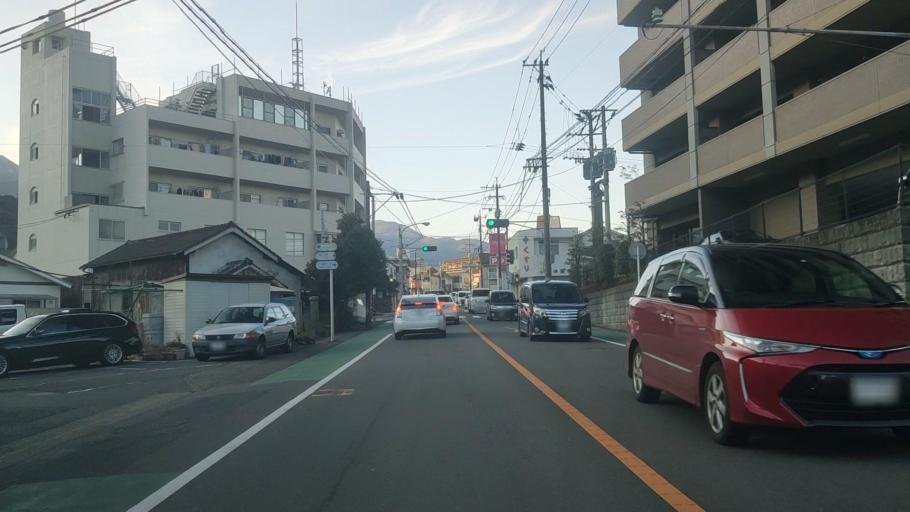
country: JP
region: Oita
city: Beppu
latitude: 33.2766
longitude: 131.4912
